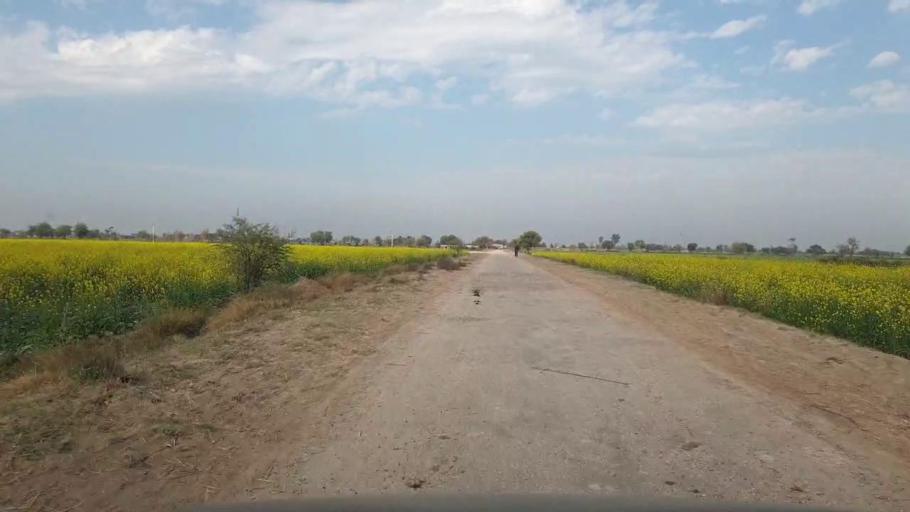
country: PK
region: Sindh
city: Hala
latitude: 26.0048
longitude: 68.4150
